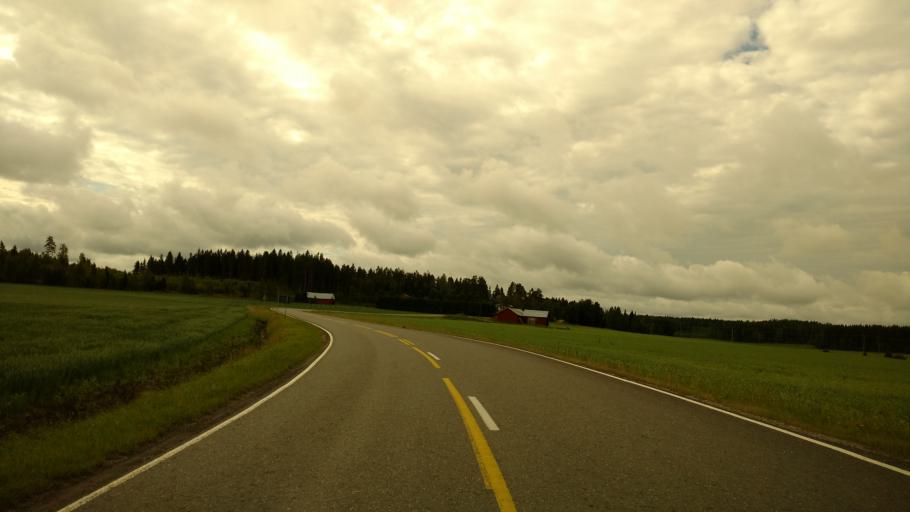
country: FI
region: Varsinais-Suomi
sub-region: Salo
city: Kuusjoki
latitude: 60.5102
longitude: 23.1798
